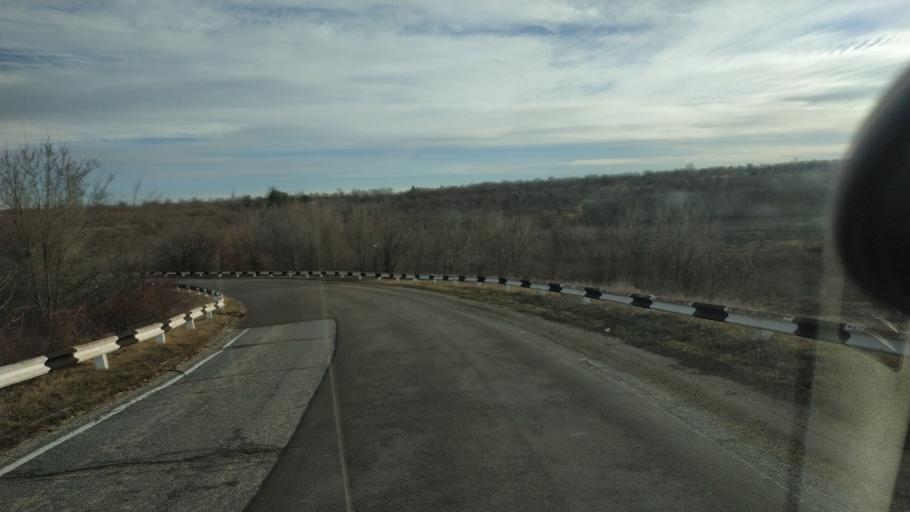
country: MD
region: Chisinau
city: Vadul lui Voda
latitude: 47.0695
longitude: 29.0199
